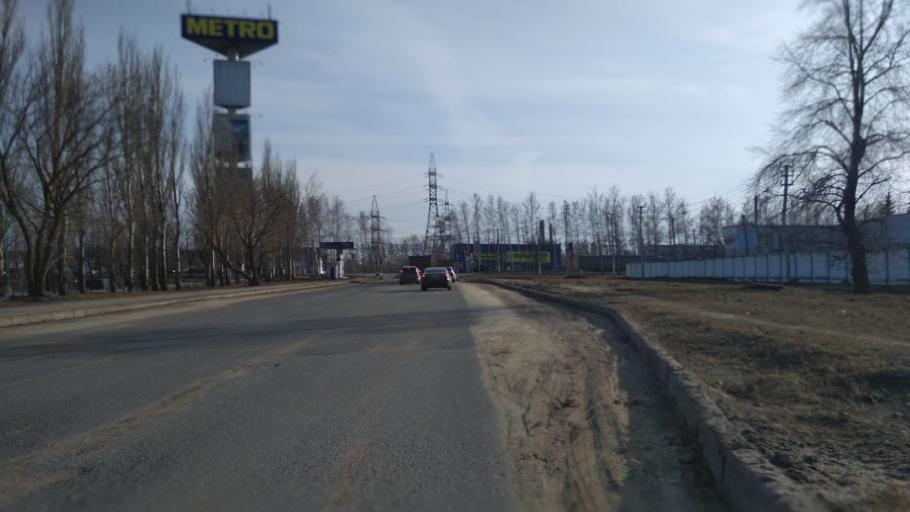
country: RU
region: Chuvashia
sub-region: Cheboksarskiy Rayon
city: Cheboksary
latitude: 56.1295
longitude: 47.3169
